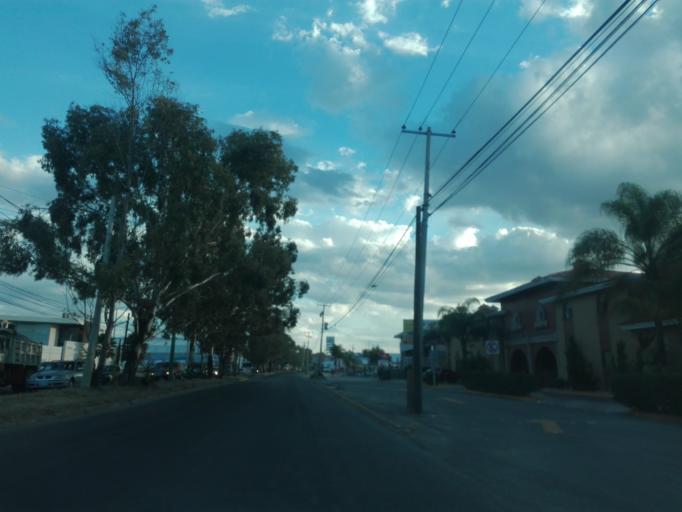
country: MX
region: Guanajuato
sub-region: Leon
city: San Jose de Duran (Los Troncoso)
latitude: 21.0838
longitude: -101.6800
